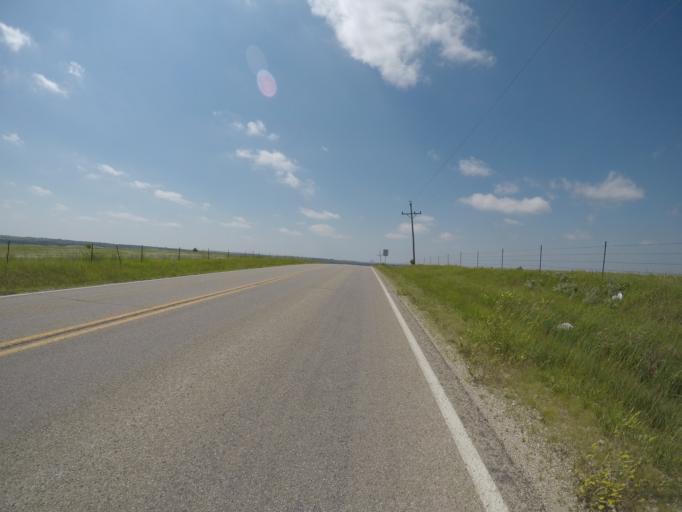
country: US
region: Kansas
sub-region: Pottawatomie County
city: Westmoreland
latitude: 39.3862
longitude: -96.4266
